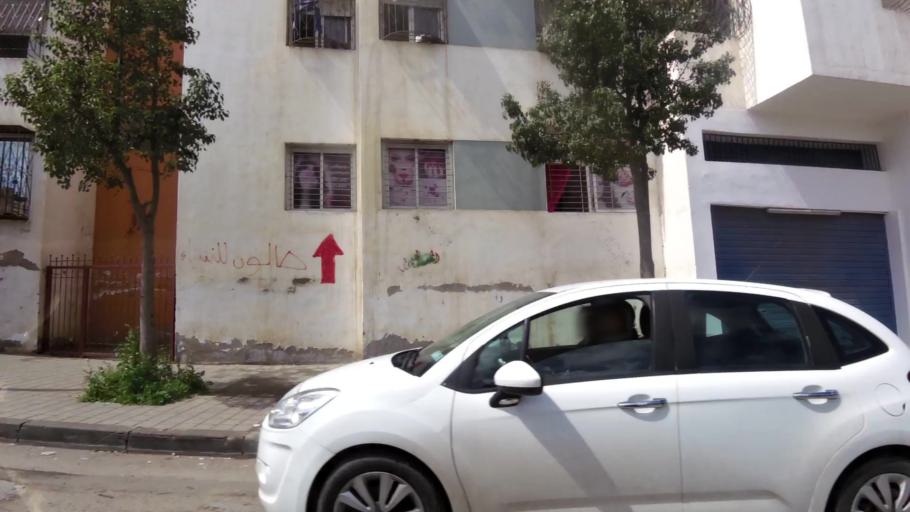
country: MA
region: Grand Casablanca
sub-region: Nouaceur
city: Dar Bouazza
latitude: 33.5377
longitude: -7.7179
